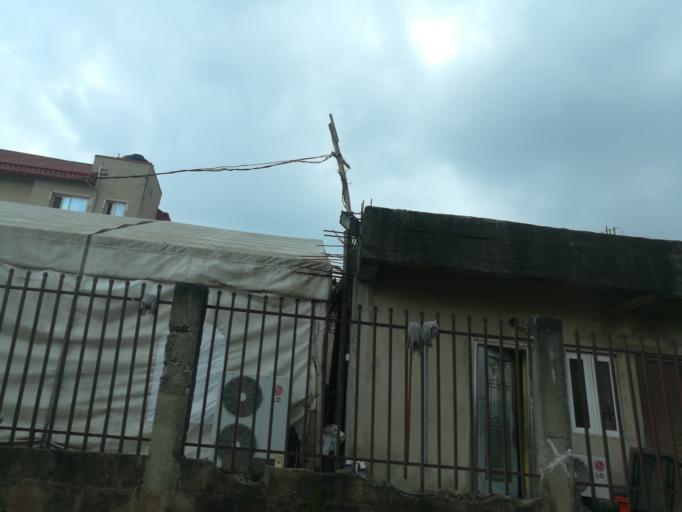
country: NG
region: Lagos
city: Ojota
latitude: 6.6025
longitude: 3.3664
